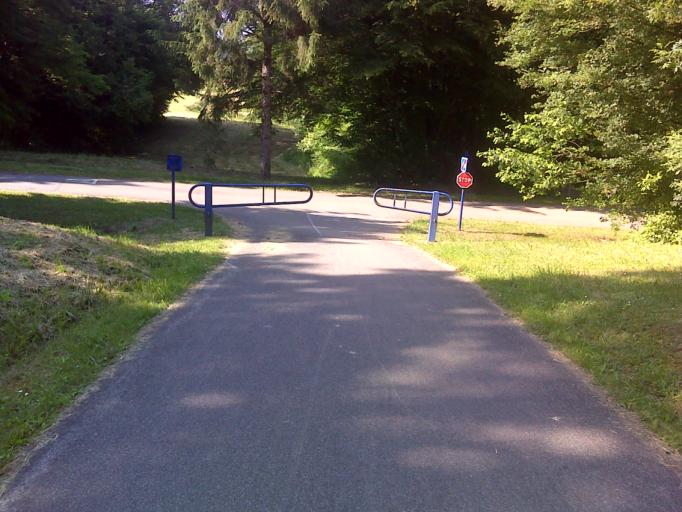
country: FR
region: Champagne-Ardenne
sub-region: Departement de la Haute-Marne
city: Villiers-en-Lieu
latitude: 48.5777
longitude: 4.8527
